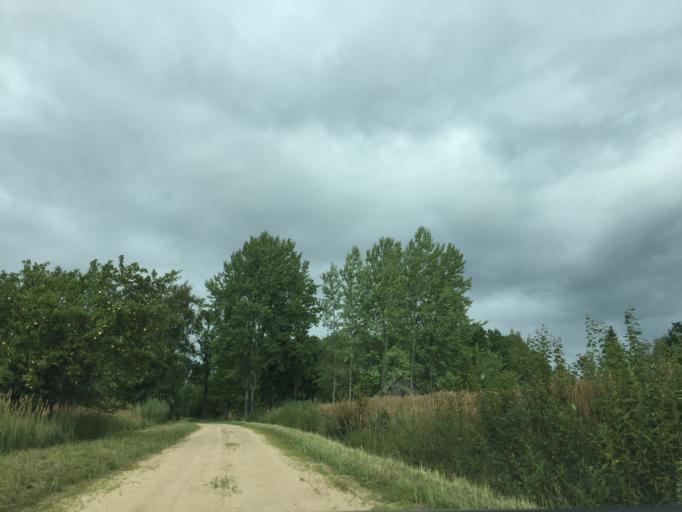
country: LV
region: Pargaujas
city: Stalbe
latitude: 57.5056
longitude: 24.9174
